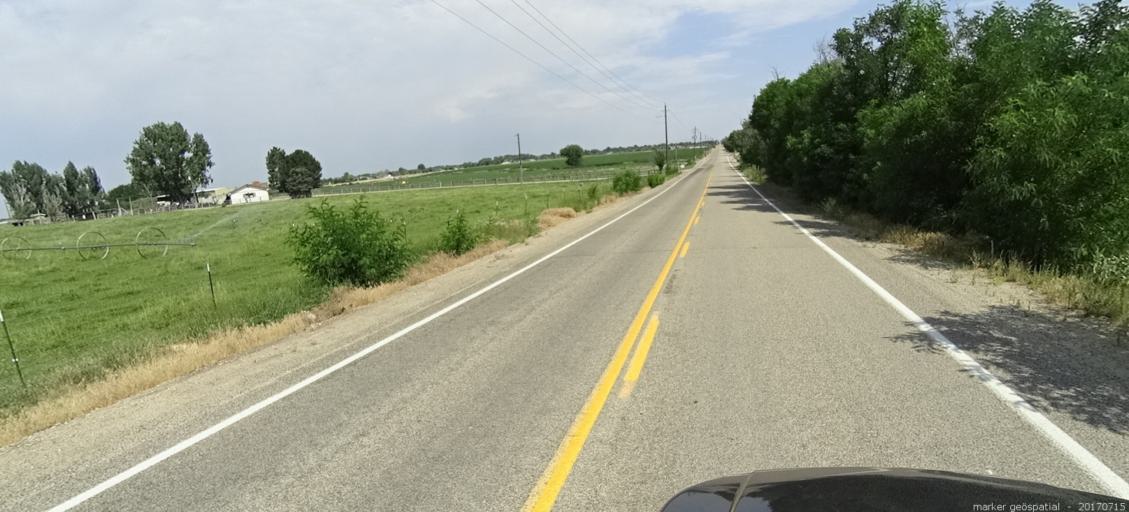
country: US
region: Idaho
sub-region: Ada County
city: Garden City
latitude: 43.5304
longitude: -116.2742
